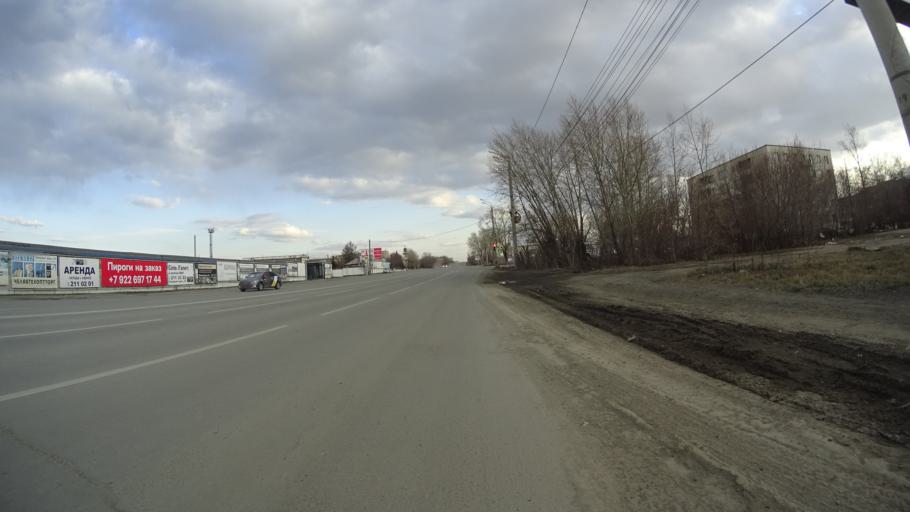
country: RU
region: Chelyabinsk
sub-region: Gorod Chelyabinsk
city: Chelyabinsk
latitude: 55.1080
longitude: 61.3869
